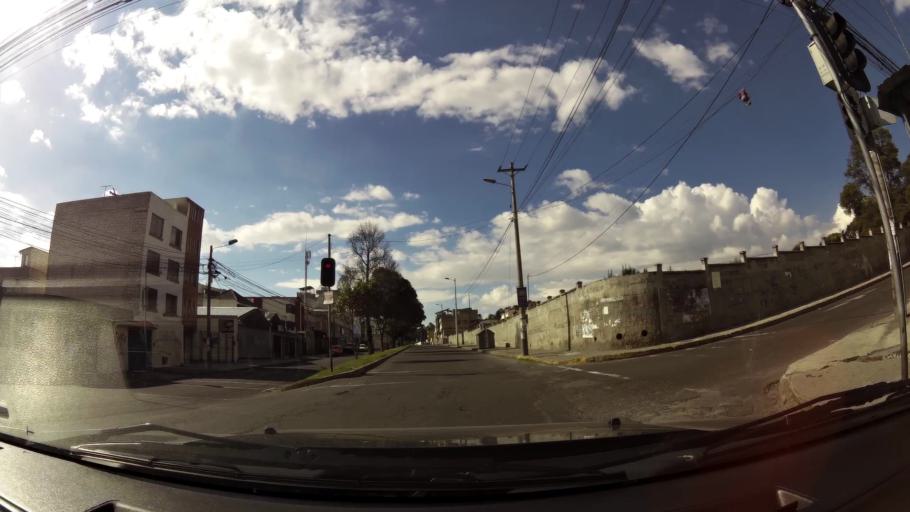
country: EC
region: Pichincha
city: Quito
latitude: -0.1156
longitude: -78.4832
